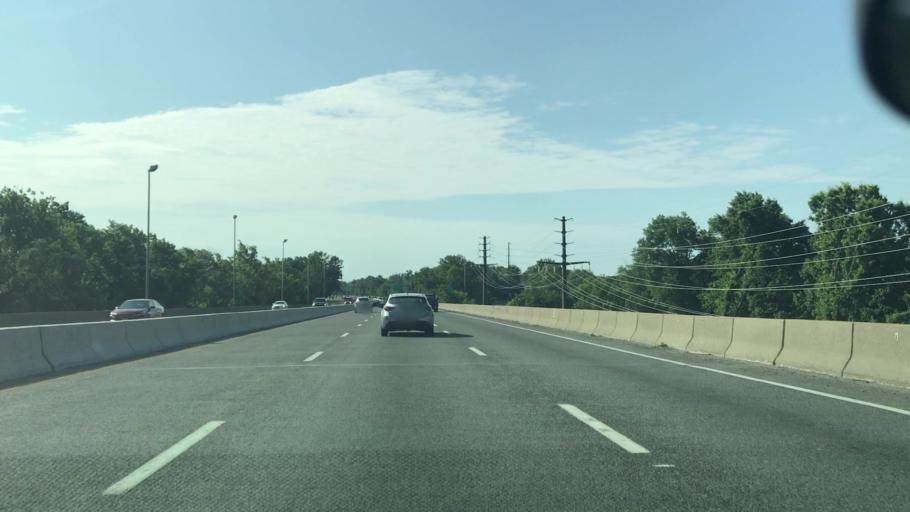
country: US
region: New Jersey
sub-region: Somerset County
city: South Bound Brook
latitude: 40.5554
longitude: -74.5455
